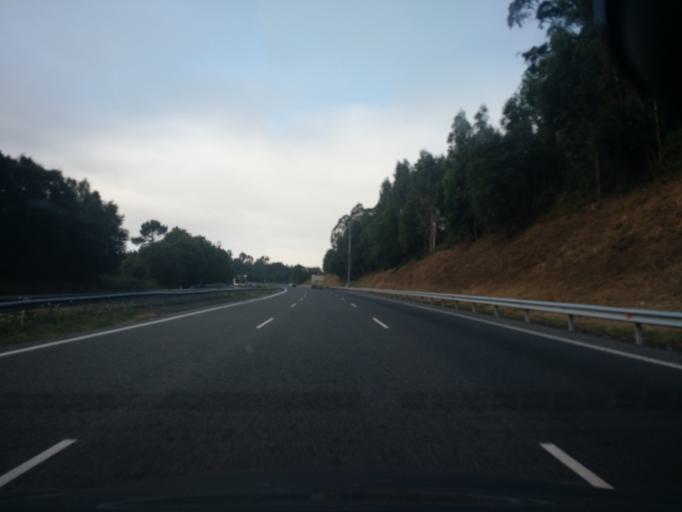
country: ES
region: Galicia
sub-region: Provincia da Coruna
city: Abegondo
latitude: 43.1856
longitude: -8.3114
